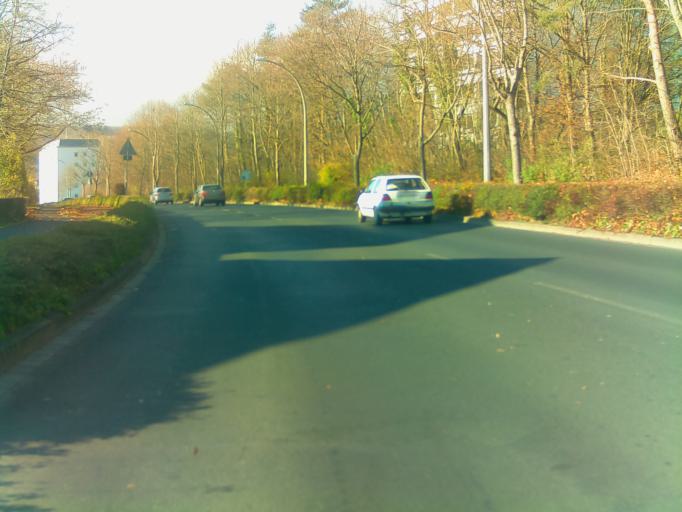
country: DE
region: Bavaria
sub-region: Regierungsbezirk Unterfranken
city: Bad Kissingen
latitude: 50.2048
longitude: 10.0867
